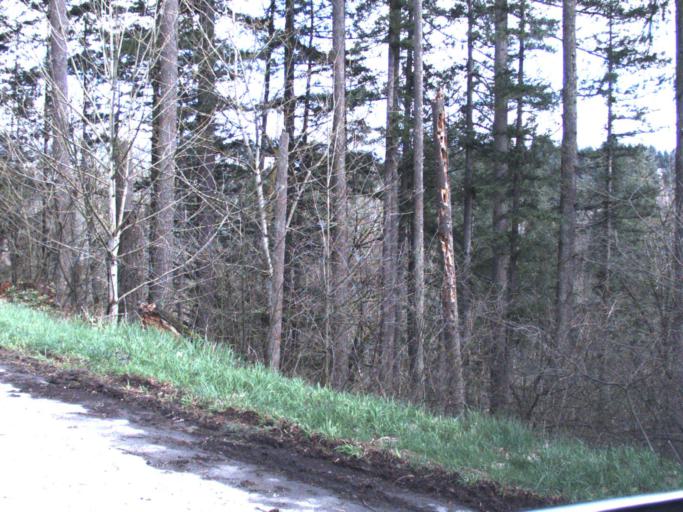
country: US
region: Washington
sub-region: King County
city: Maple Valley
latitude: 47.3996
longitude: -122.0442
